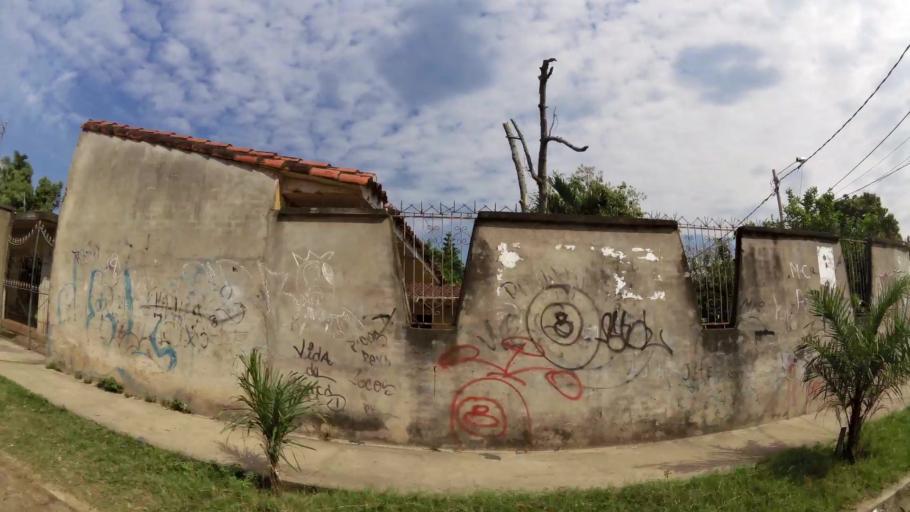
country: BO
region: Santa Cruz
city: Santa Cruz de la Sierra
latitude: -17.7271
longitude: -63.1805
